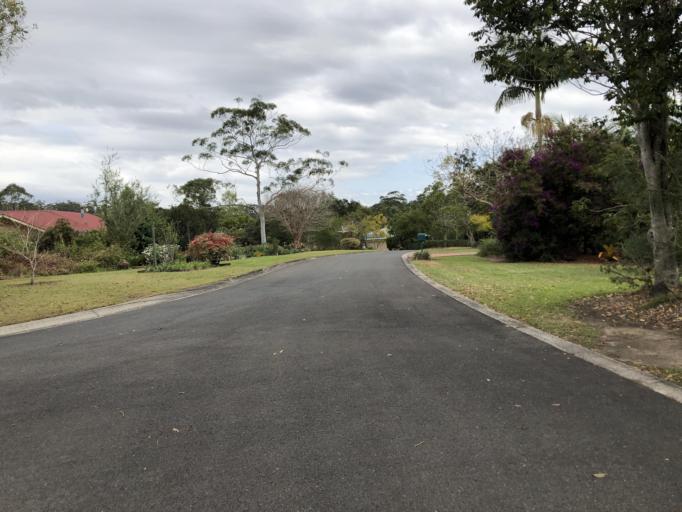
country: AU
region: Queensland
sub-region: Sunshine Coast
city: Black Mountain
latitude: -26.3455
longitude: 152.8879
